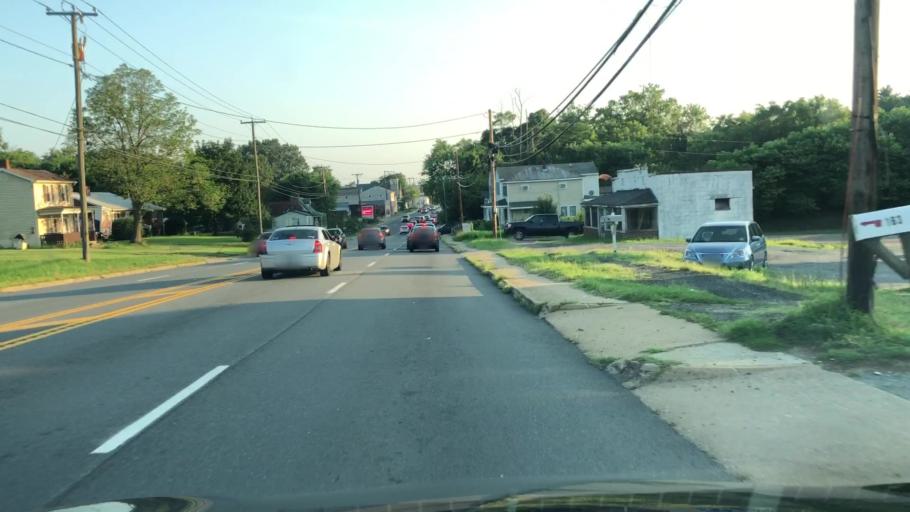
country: US
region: Virginia
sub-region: Stafford County
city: Falmouth
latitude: 38.3272
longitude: -77.4666
